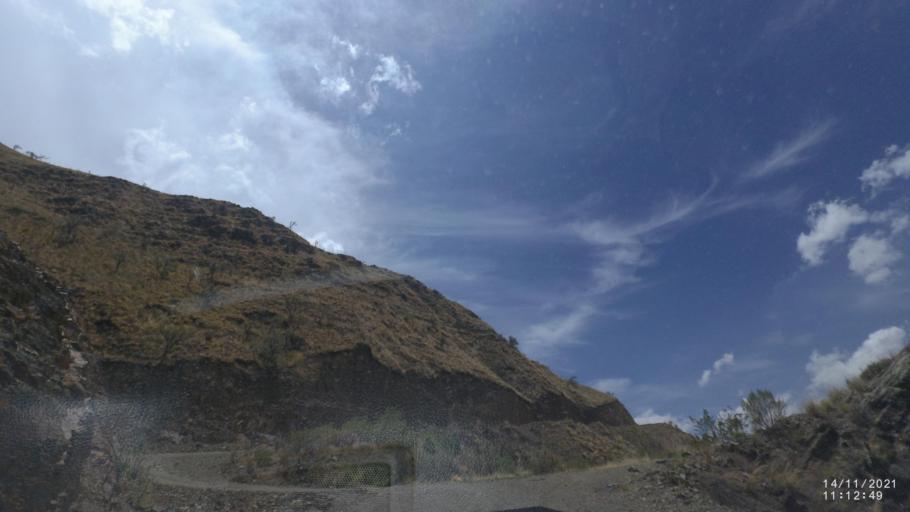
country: BO
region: Cochabamba
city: Cochabamba
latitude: -17.3263
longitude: -66.0498
